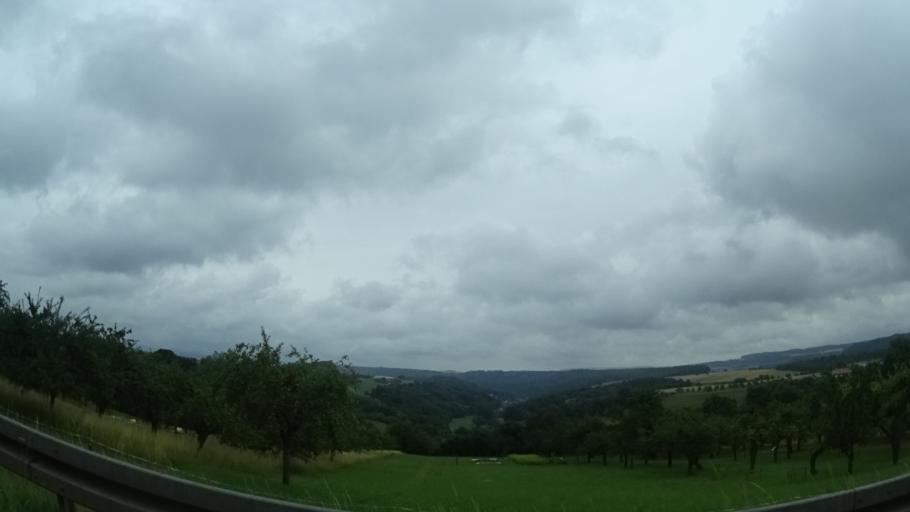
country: DE
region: Saarland
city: Orscholz
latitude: 49.4583
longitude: 6.5065
